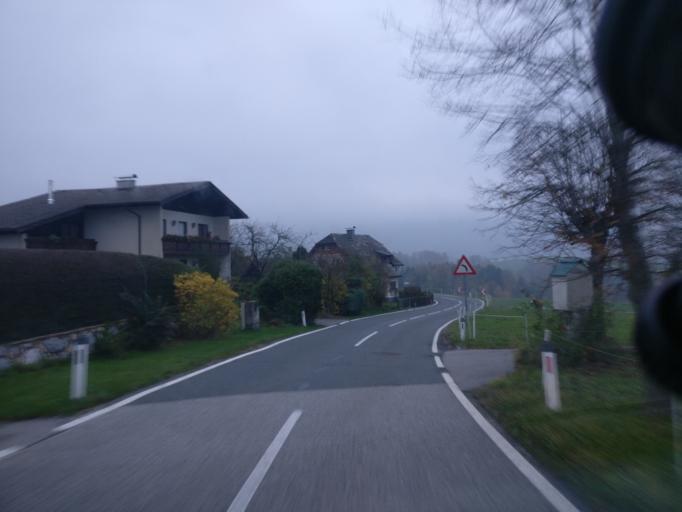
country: AT
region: Salzburg
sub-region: Politischer Bezirk Salzburg-Umgebung
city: Hallwang
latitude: 47.8633
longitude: 13.0804
